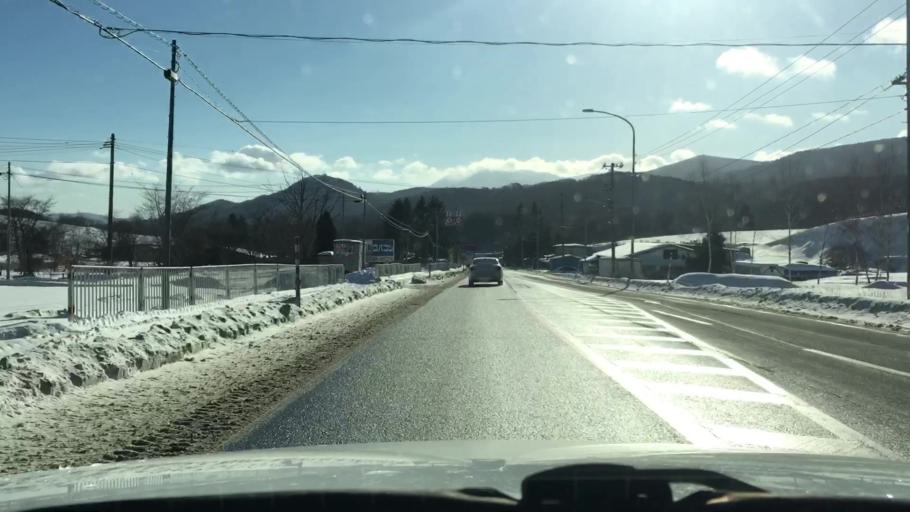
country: JP
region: Iwate
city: Morioka-shi
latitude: 39.6504
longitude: 141.3543
